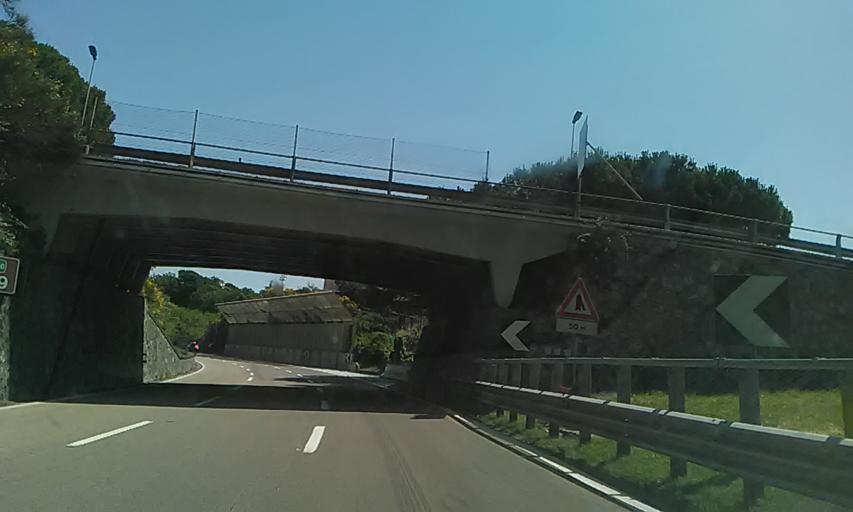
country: IT
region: Liguria
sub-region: Provincia di Savona
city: Celle Ligure
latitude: 44.3480
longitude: 8.5560
